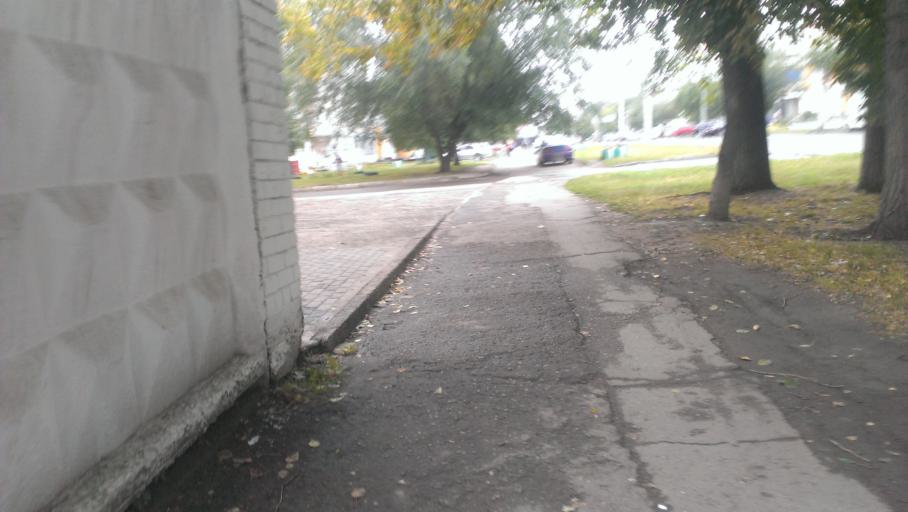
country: RU
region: Altai Krai
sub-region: Gorod Barnaulskiy
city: Barnaul
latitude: 53.3707
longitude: 83.6837
